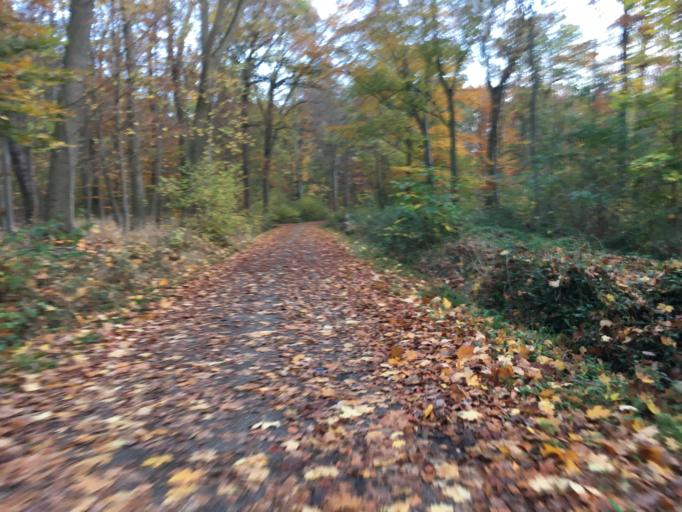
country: DE
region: Baden-Wuerttemberg
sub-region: Regierungsbezirk Stuttgart
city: Weinsberg
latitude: 49.1444
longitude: 9.2668
